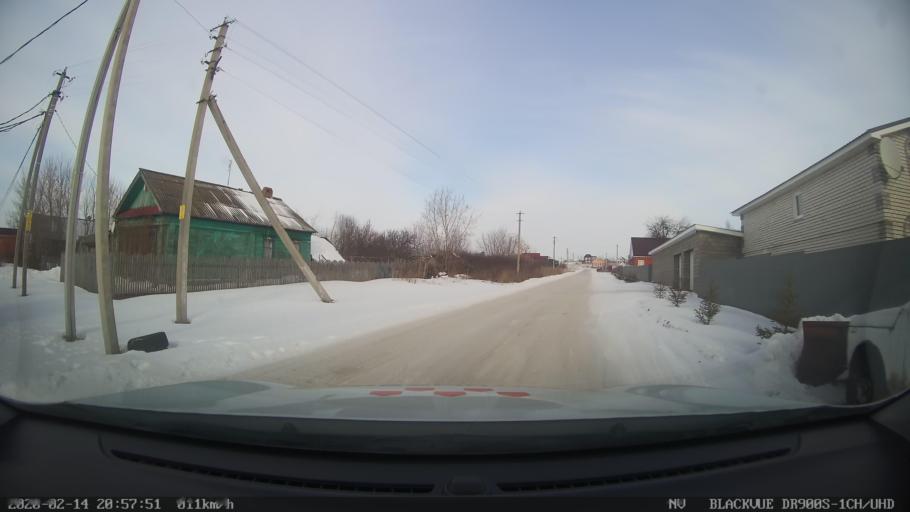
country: RU
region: Tatarstan
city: Kuybyshevskiy Zaton
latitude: 55.1764
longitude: 49.2473
